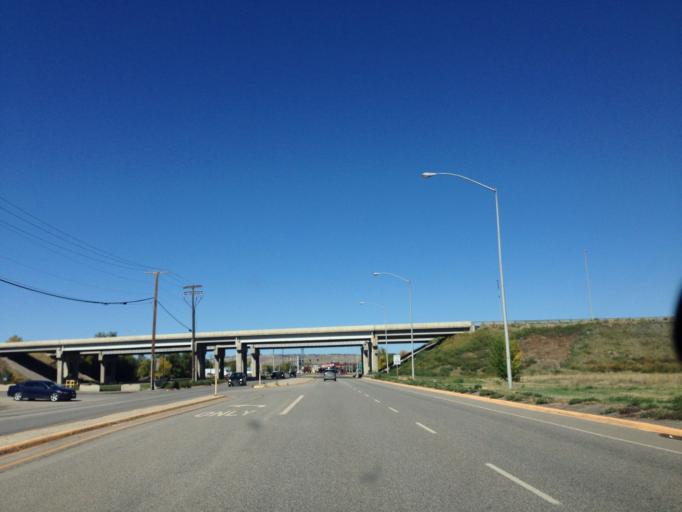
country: US
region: Montana
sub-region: Yellowstone County
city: Laurel
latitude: 45.6616
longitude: -108.7681
